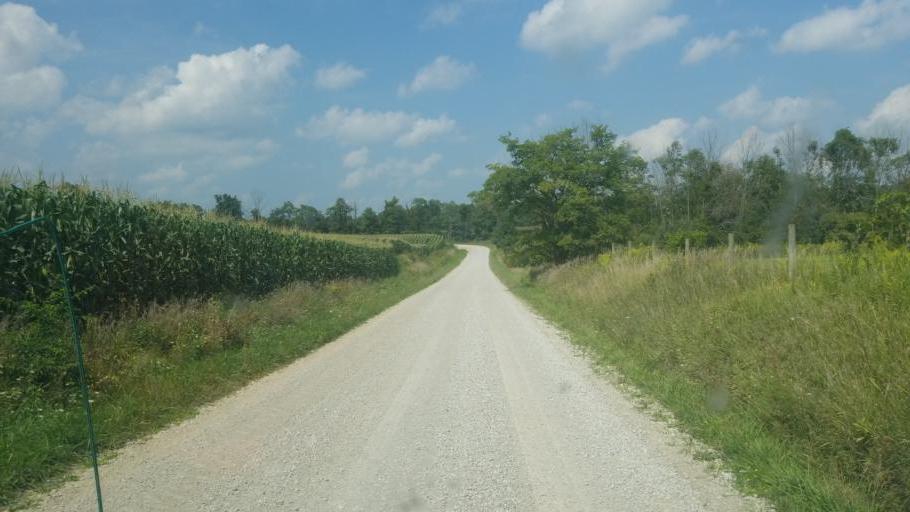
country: US
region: Ohio
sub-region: Huron County
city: New London
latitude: 40.9843
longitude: -82.4082
